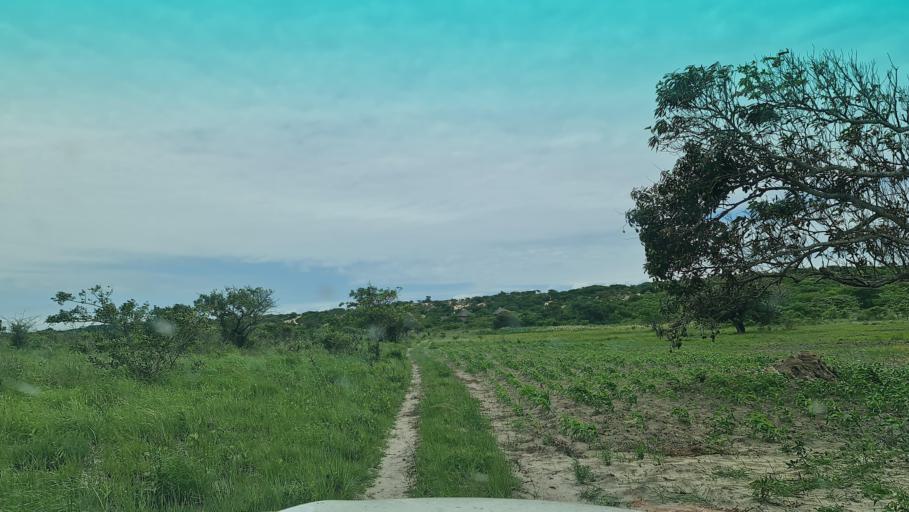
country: EG
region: Luxor
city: Luxor
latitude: 25.6379
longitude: 32.7718
